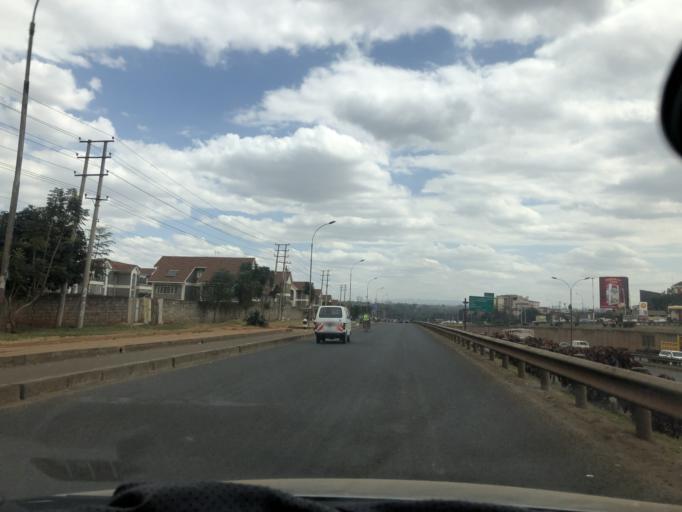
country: KE
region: Nairobi Area
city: Pumwani
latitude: -1.2321
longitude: 36.8768
